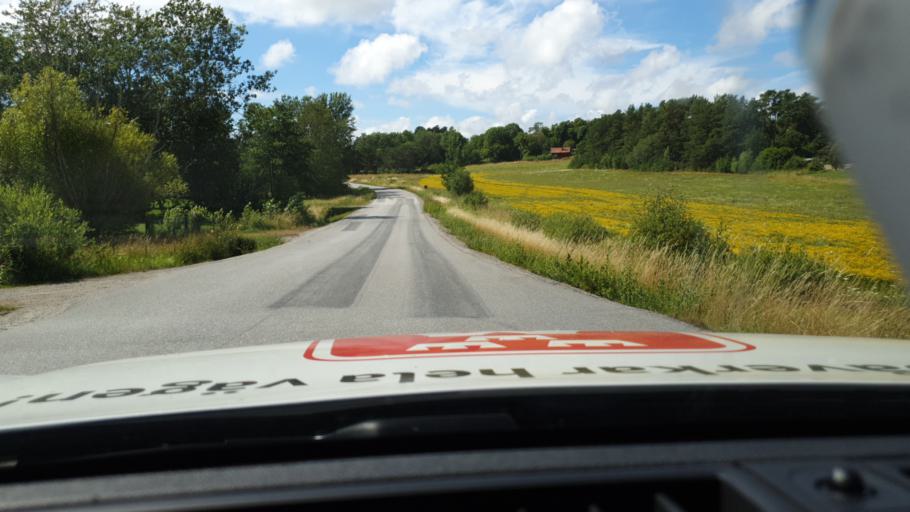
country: SE
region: Stockholm
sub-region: Haninge Kommun
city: Jordbro
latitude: 59.0208
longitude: 18.1451
